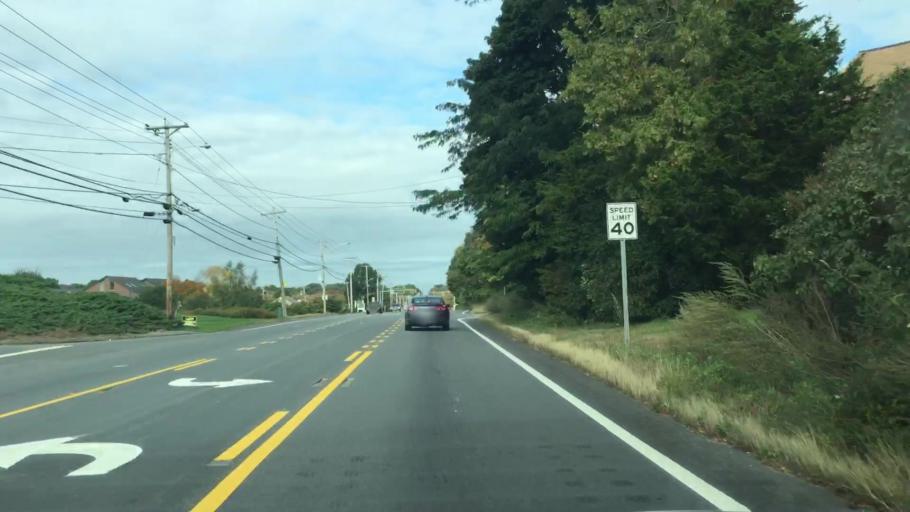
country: US
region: Massachusetts
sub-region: Essex County
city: Andover
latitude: 42.6570
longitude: -71.1035
